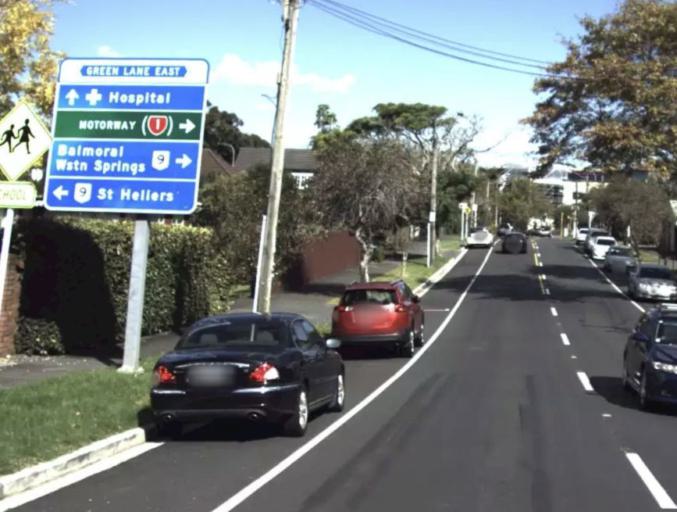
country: NZ
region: Auckland
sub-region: Auckland
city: Auckland
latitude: -36.8847
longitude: 174.8017
